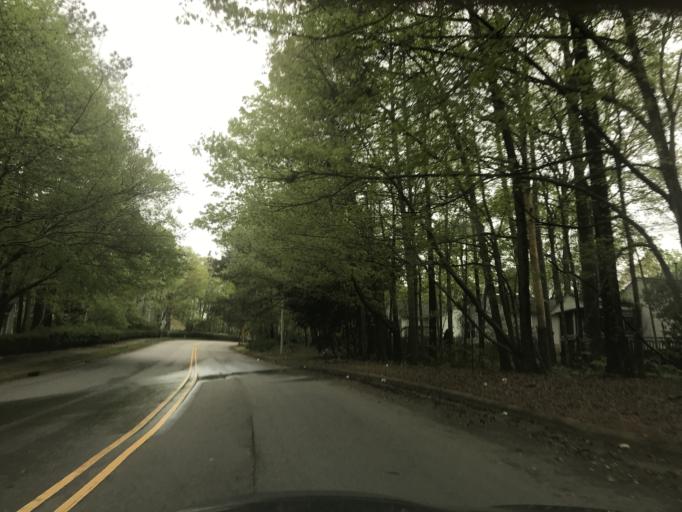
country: US
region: North Carolina
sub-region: Wake County
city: West Raleigh
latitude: 35.7500
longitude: -78.6876
